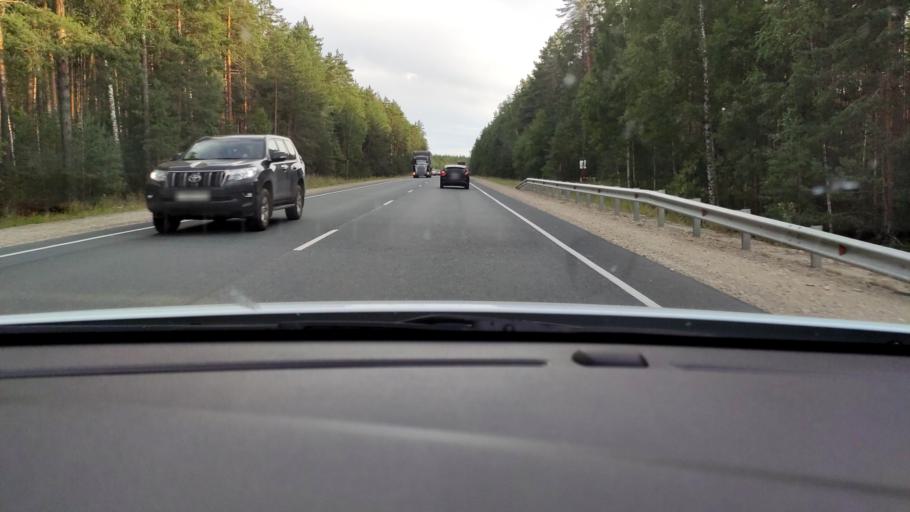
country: RU
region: Mariy-El
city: Pomary
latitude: 56.0365
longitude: 48.3799
